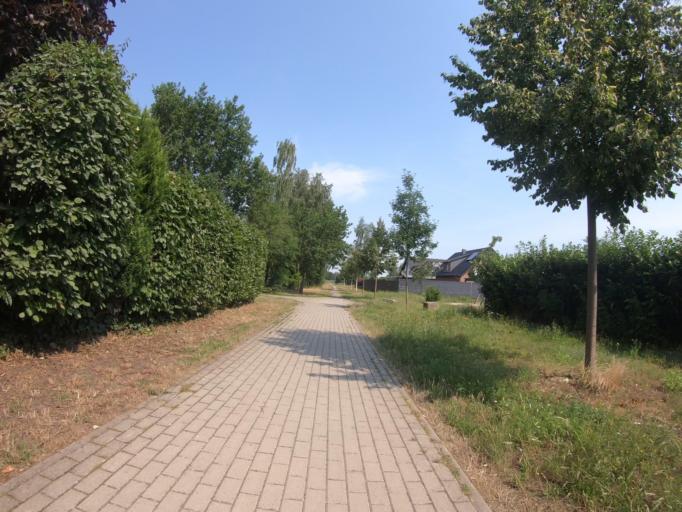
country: DE
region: Lower Saxony
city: Wagenhoff
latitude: 52.4992
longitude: 10.5196
